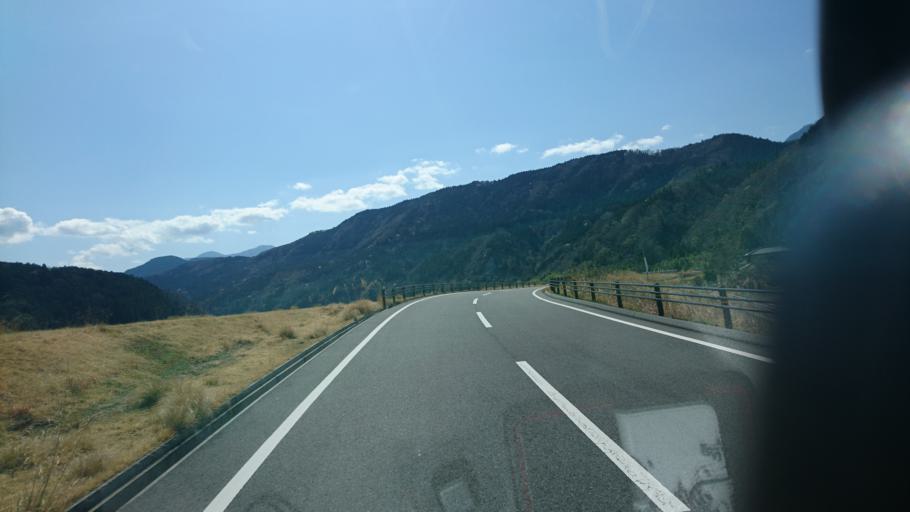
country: JP
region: Shizuoka
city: Fujinomiya
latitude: 35.3606
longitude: 138.4467
